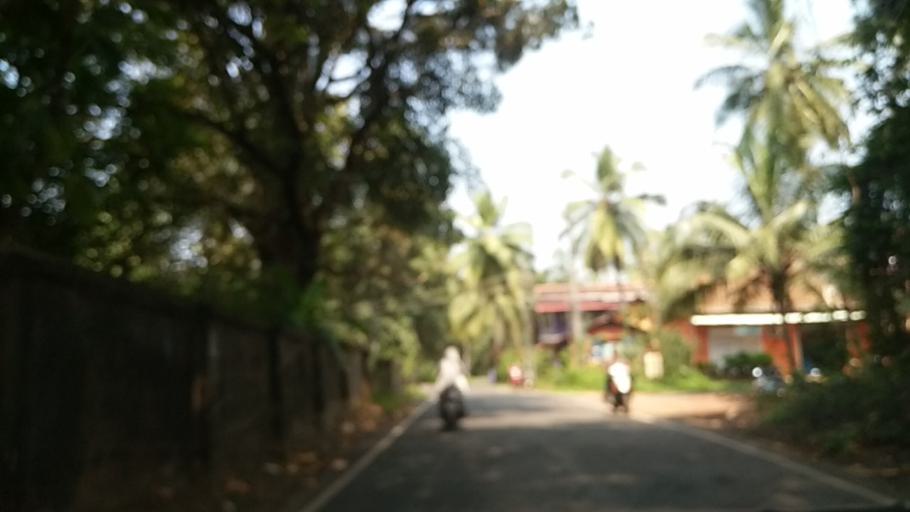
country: IN
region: Goa
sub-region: South Goa
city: Colva
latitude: 15.2845
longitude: 73.9204
